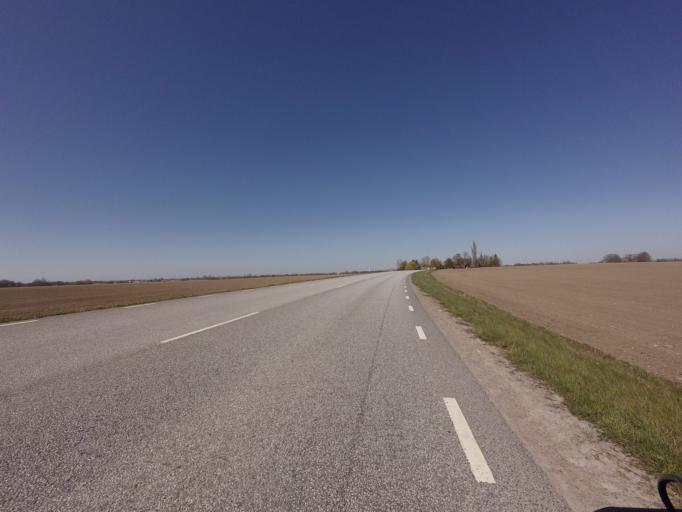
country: SE
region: Skane
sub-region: Vellinge Kommun
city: Vellinge
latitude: 55.4666
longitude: 13.0573
